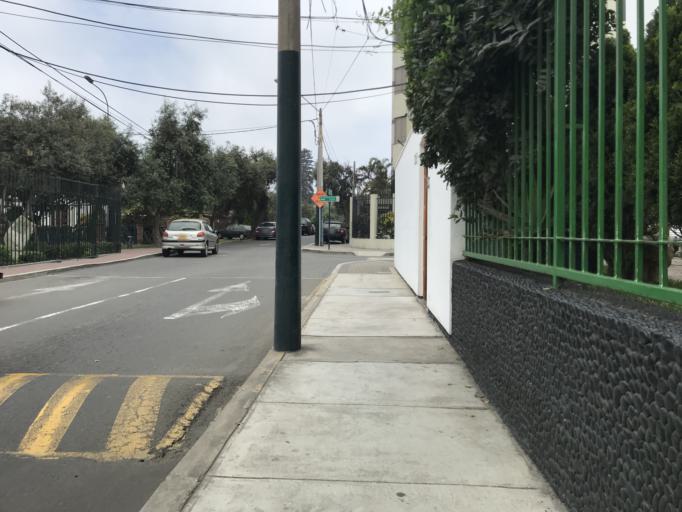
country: PE
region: Lima
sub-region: Lima
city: San Isidro
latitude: -12.1011
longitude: -77.0337
